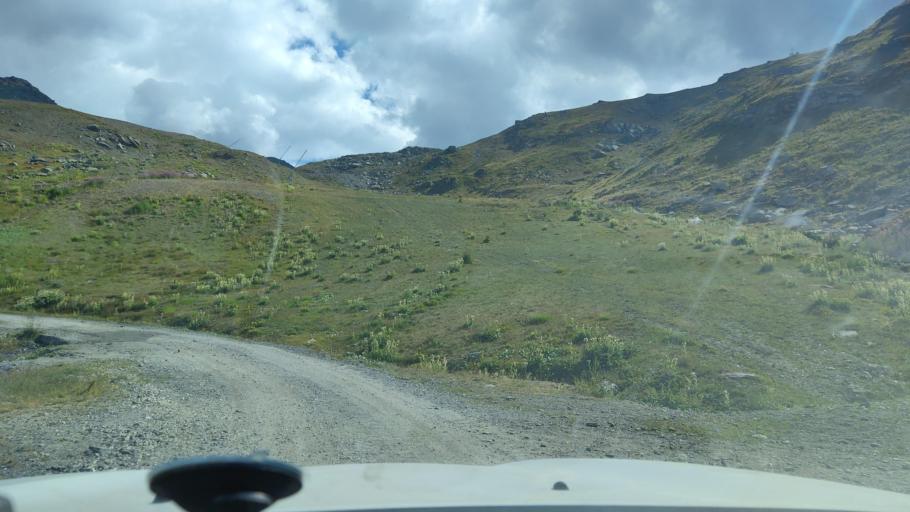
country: FR
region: Rhone-Alpes
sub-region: Departement de la Savoie
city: Val Thorens
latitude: 45.2818
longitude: 6.5810
